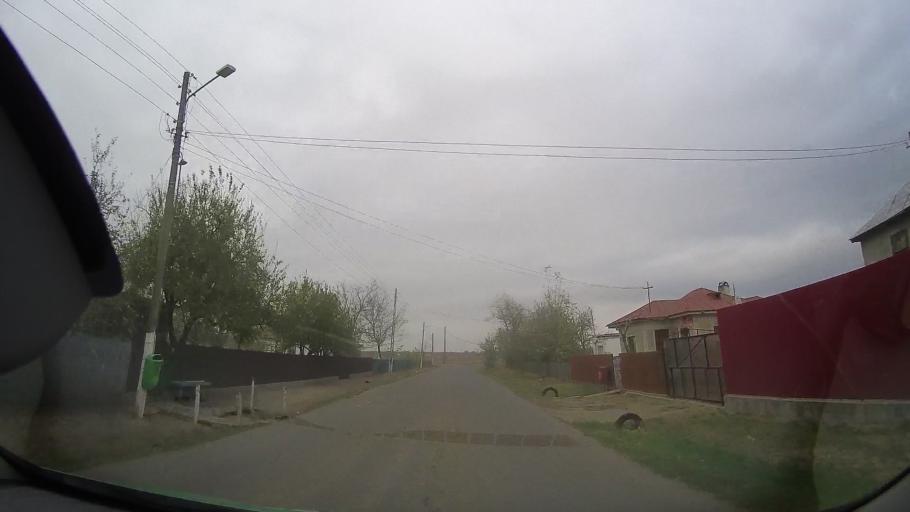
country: RO
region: Braila
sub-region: Comuna Ciocile
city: Ciocile
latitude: 44.7869
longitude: 27.2692
